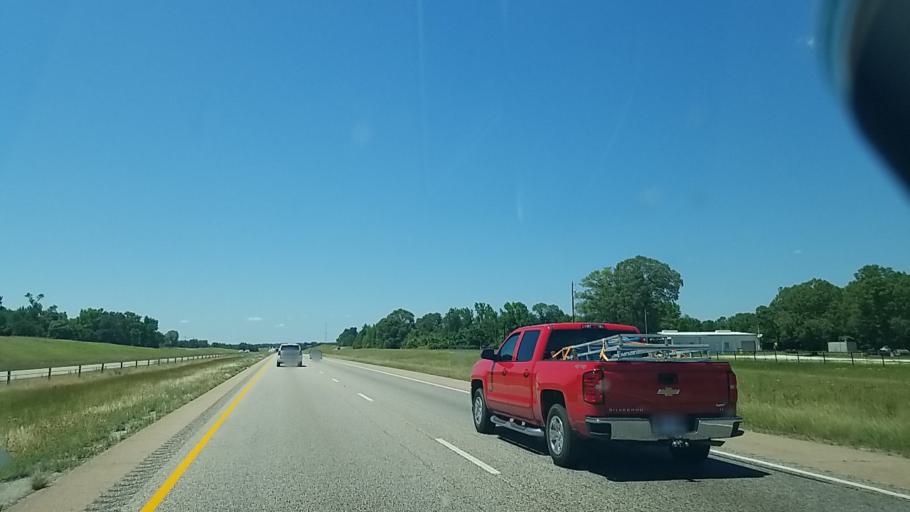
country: US
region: Texas
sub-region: Leon County
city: Buffalo
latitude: 31.4000
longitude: -96.0348
